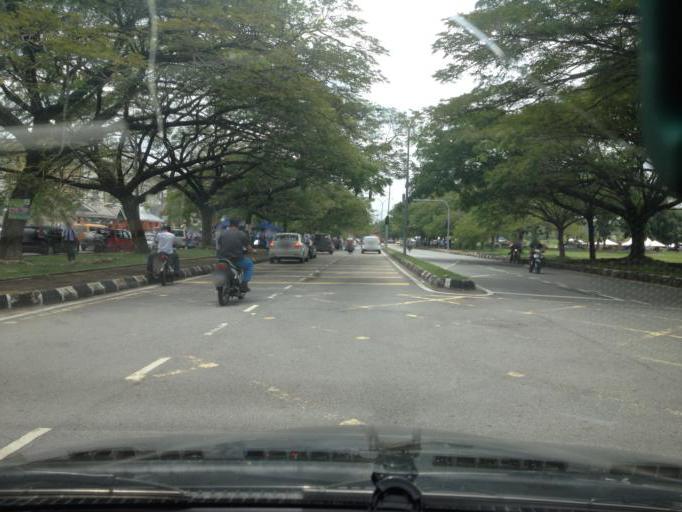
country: MY
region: Kedah
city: Sungai Petani
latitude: 5.6086
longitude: 100.5337
